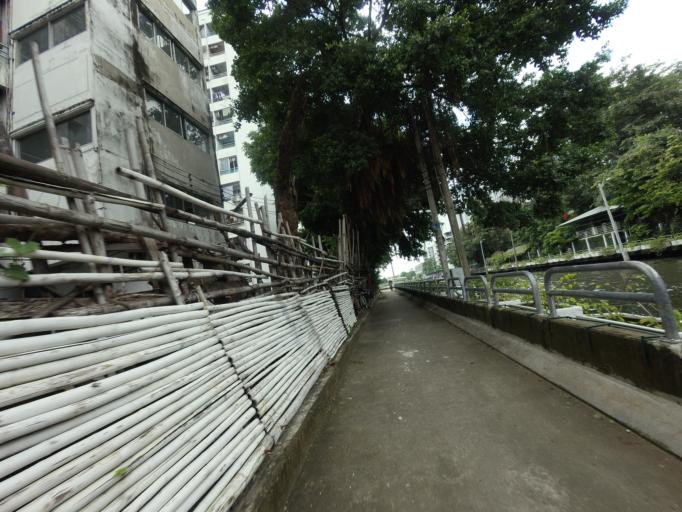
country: TH
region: Bangkok
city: Bang Kapi
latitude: 13.7645
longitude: 100.6447
